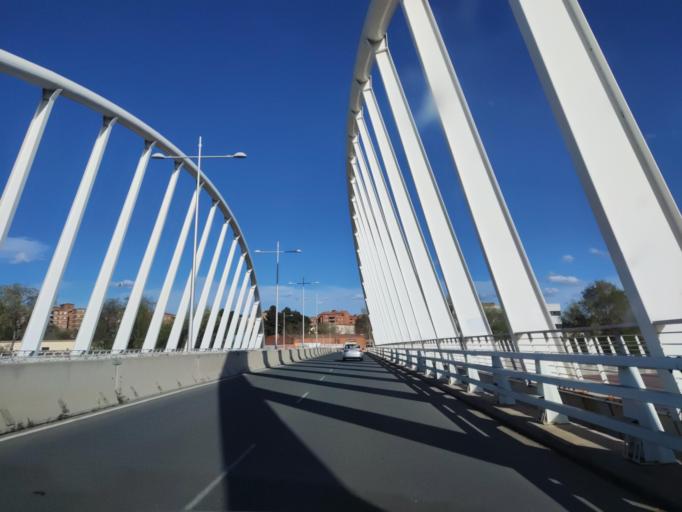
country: ES
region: Castille-La Mancha
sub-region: Province of Toledo
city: Toledo
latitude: 39.8740
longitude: -4.0447
